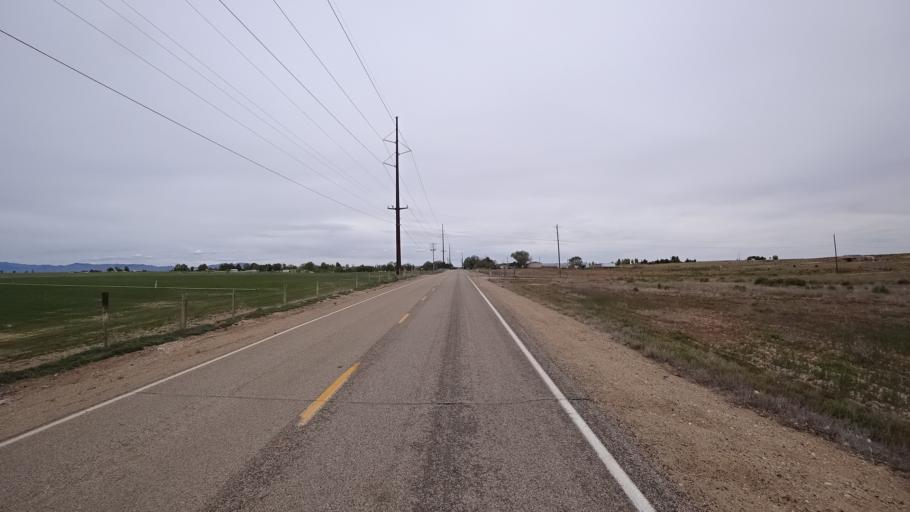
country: US
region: Idaho
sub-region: Ada County
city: Kuna
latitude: 43.4883
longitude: -116.3103
